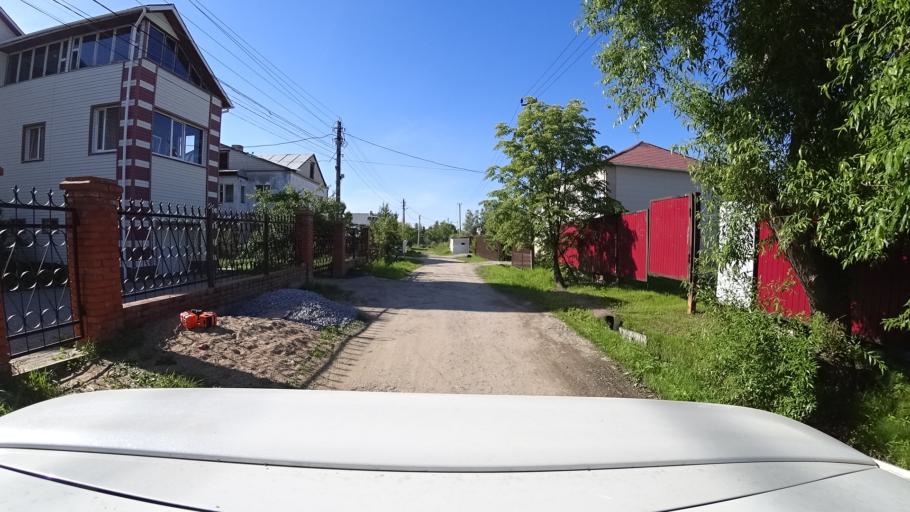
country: RU
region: Khabarovsk Krai
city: Topolevo
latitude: 48.5423
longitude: 135.1754
